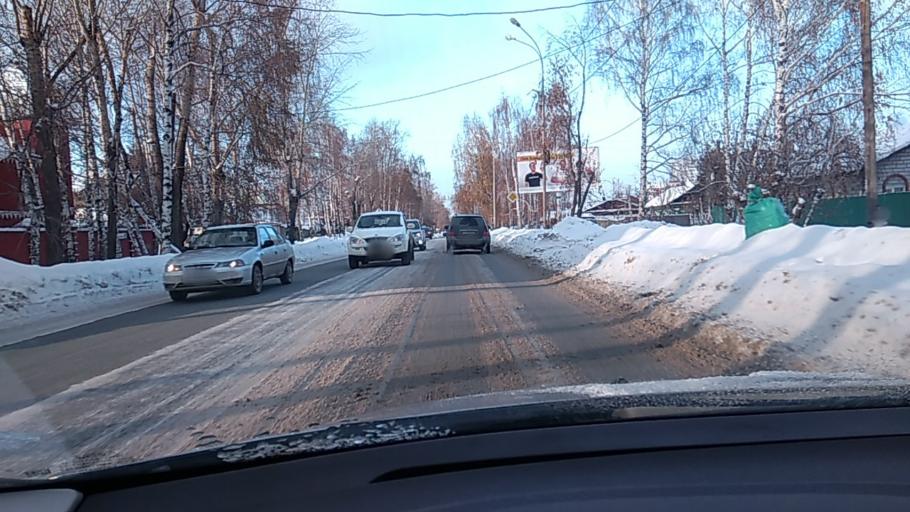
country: RU
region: Sverdlovsk
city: Yekaterinburg
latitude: 56.8073
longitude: 60.5898
